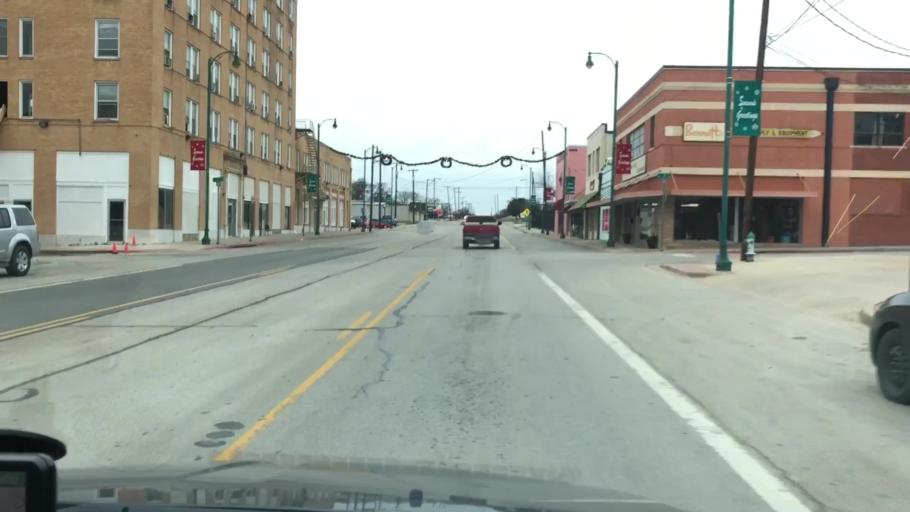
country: US
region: Texas
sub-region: Palo Pinto County
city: Mineral Wells
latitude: 32.8114
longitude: -98.1128
